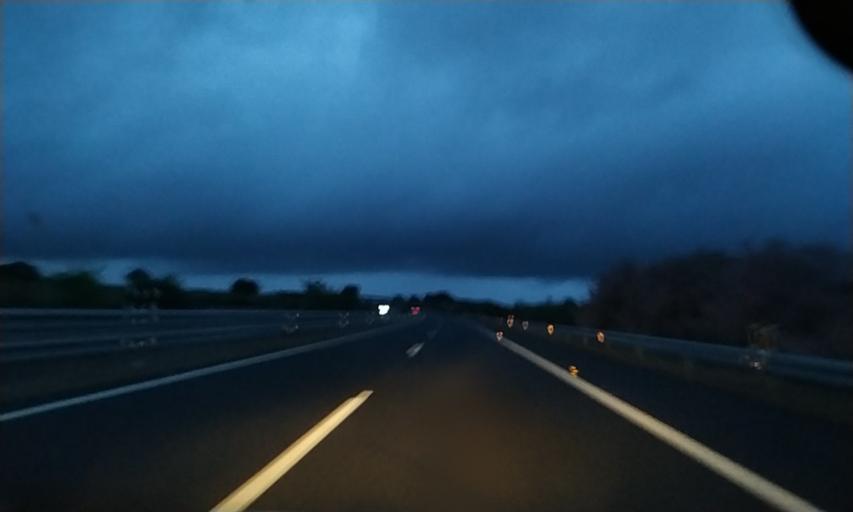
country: ES
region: Extremadura
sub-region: Provincia de Caceres
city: Aldea del Cano
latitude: 39.3096
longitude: -6.3274
